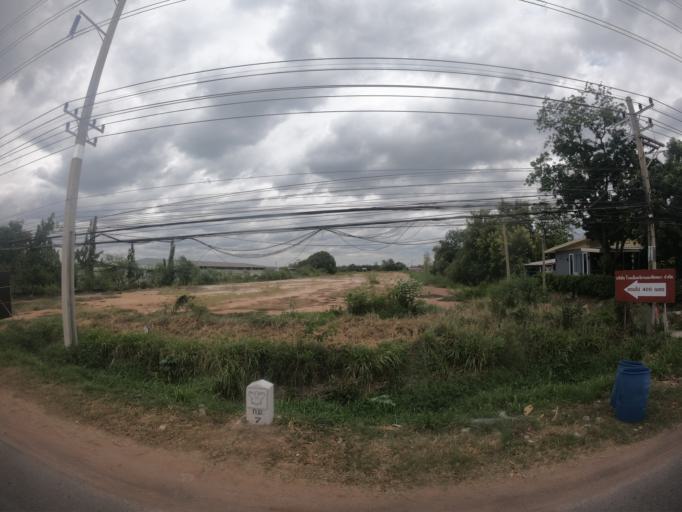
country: TH
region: Nakhon Ratchasima
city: Nakhon Ratchasima
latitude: 14.9438
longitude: 102.1291
